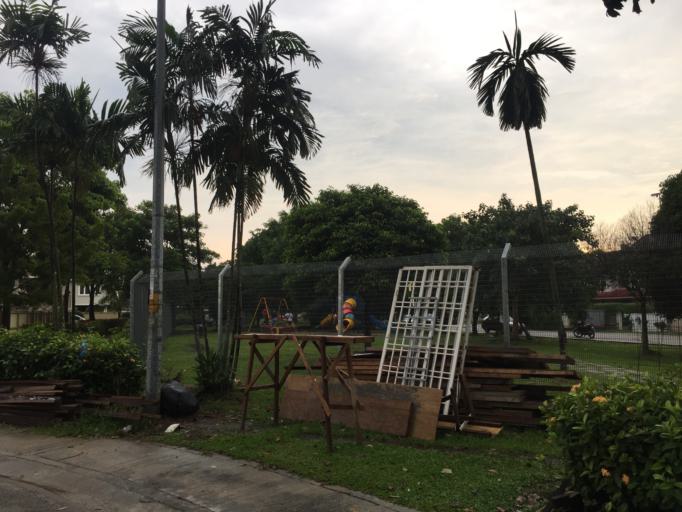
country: MY
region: Selangor
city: Klang
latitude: 2.9903
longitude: 101.4378
